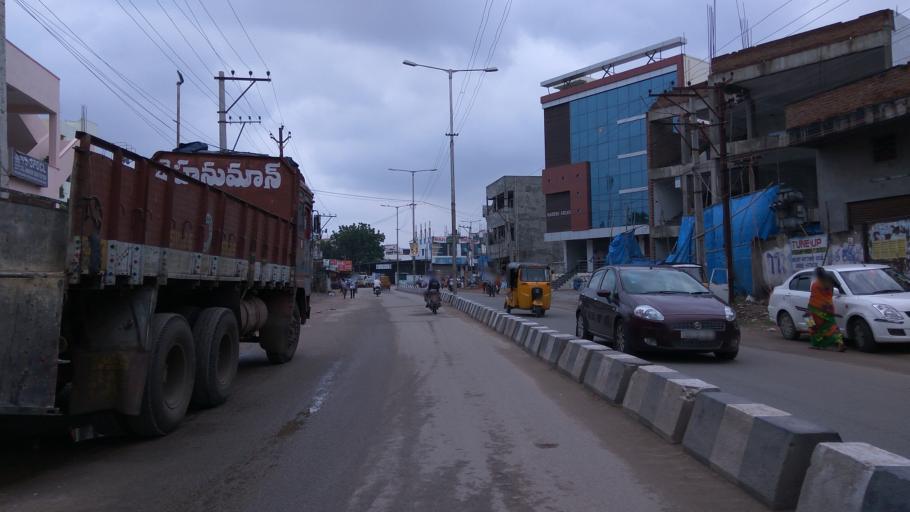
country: IN
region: Telangana
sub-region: Hyderabad
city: Malkajgiri
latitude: 17.4429
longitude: 78.5332
